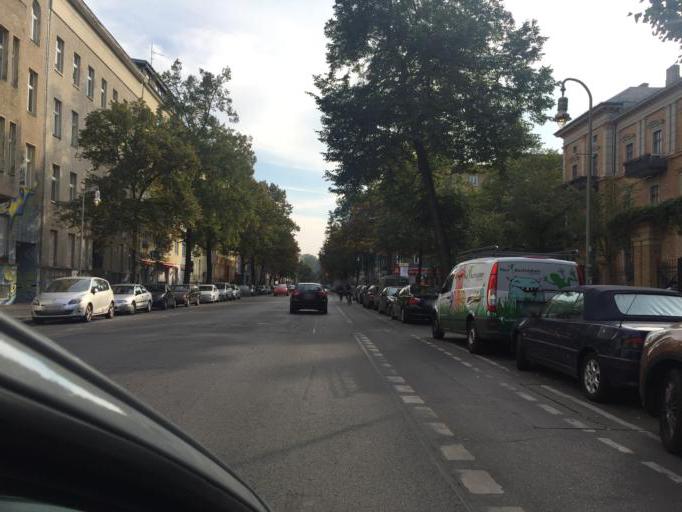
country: DE
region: Berlin
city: Bezirk Kreuzberg
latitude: 52.4959
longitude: 13.3843
